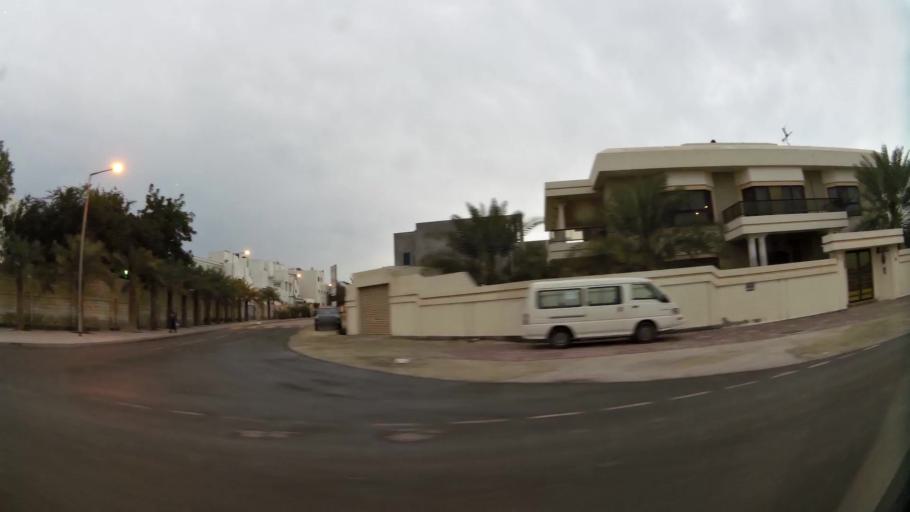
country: BH
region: Northern
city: Madinat `Isa
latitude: 26.1511
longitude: 50.5348
